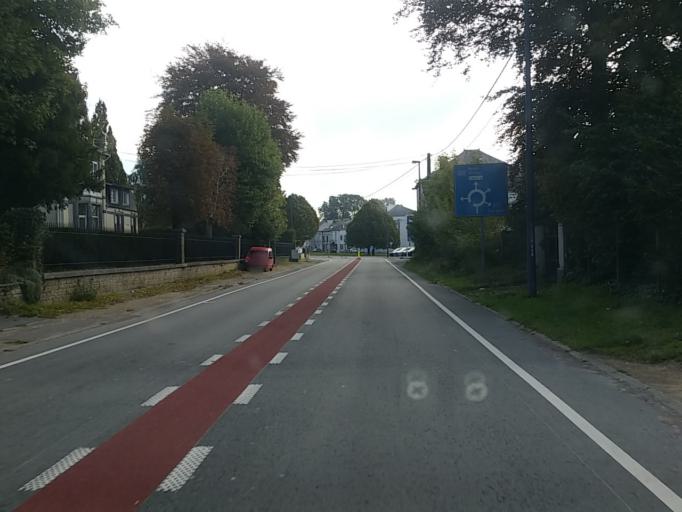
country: BE
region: Wallonia
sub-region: Province du Luxembourg
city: Florenville
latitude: 49.6974
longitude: 5.3020
